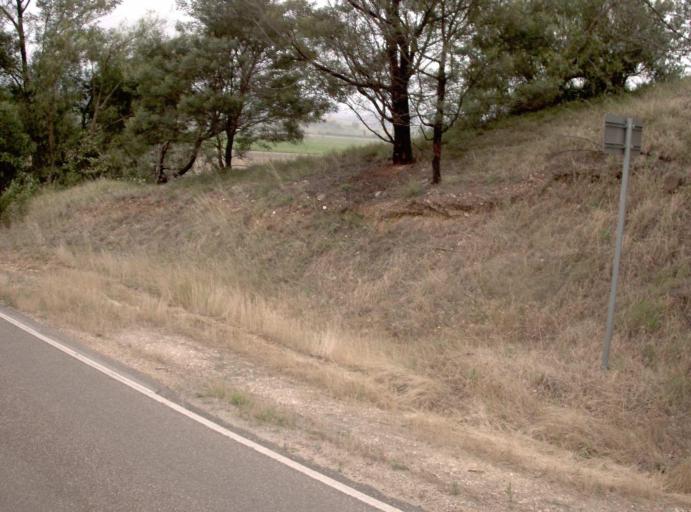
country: AU
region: Victoria
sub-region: East Gippsland
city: Bairnsdale
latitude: -37.7991
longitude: 147.4398
